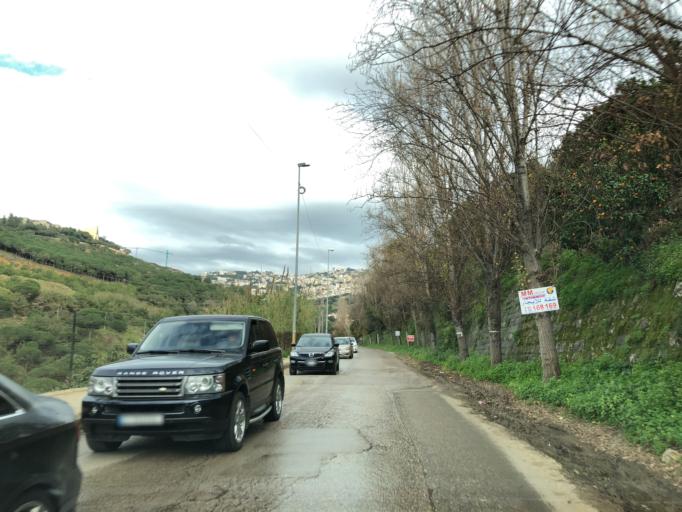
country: LB
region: Mont-Liban
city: Jdaidet el Matn
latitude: 33.8610
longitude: 35.5678
